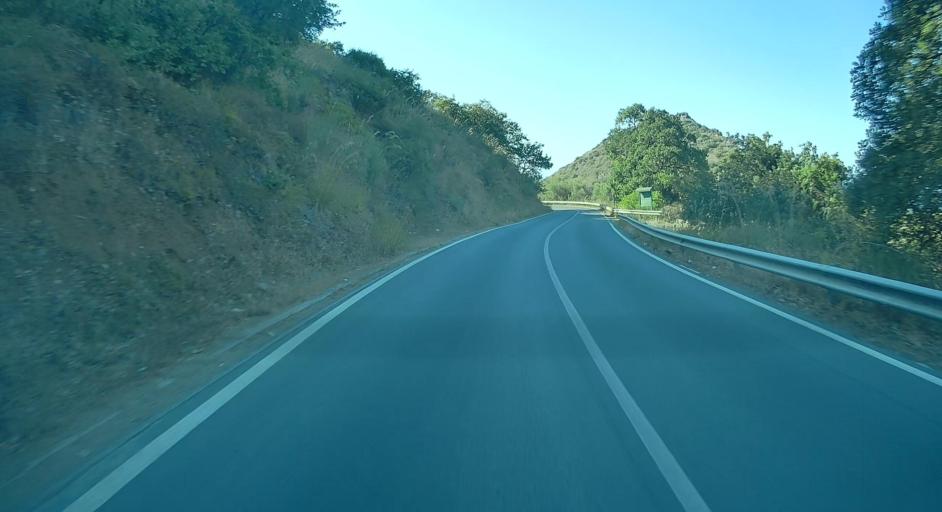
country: IT
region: Sicily
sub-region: Messina
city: Oliveri
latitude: 38.1415
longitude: 15.0285
